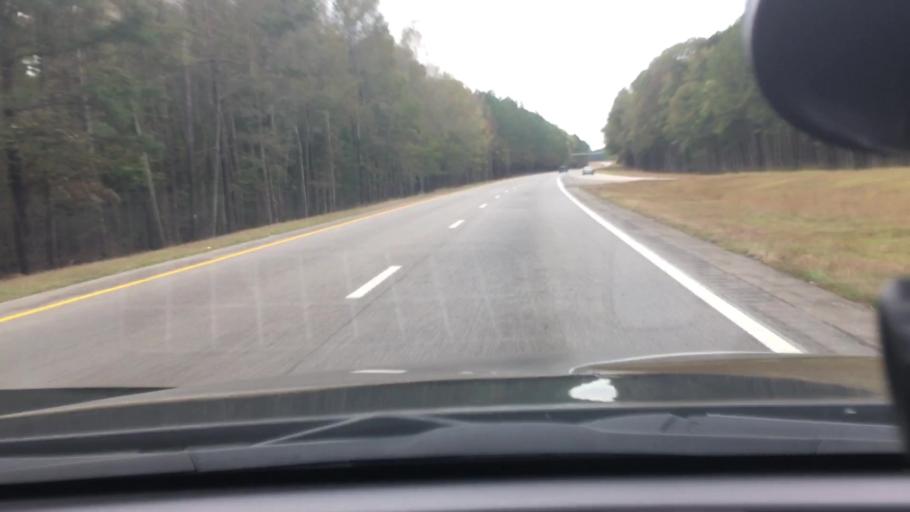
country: US
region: North Carolina
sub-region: Wake County
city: Zebulon
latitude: 35.8004
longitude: -78.1926
